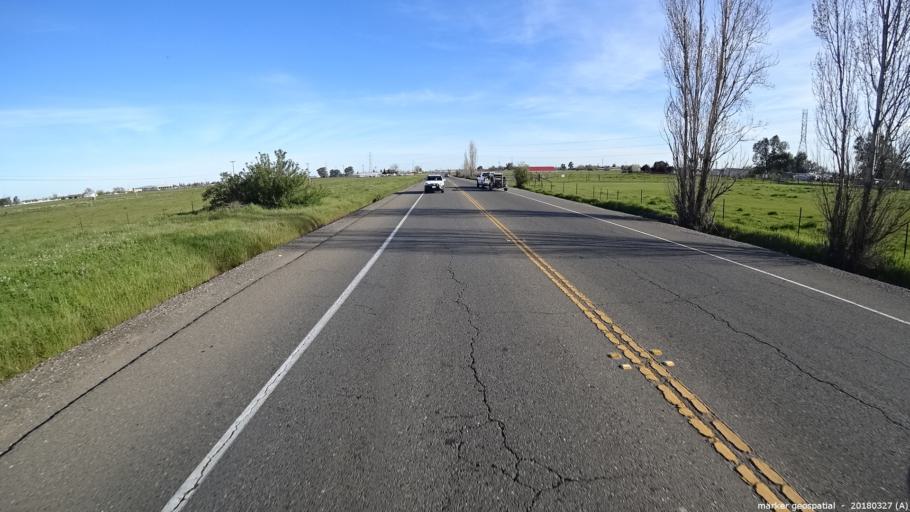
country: US
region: California
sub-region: Sacramento County
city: Florin
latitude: 38.4986
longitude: -121.3721
